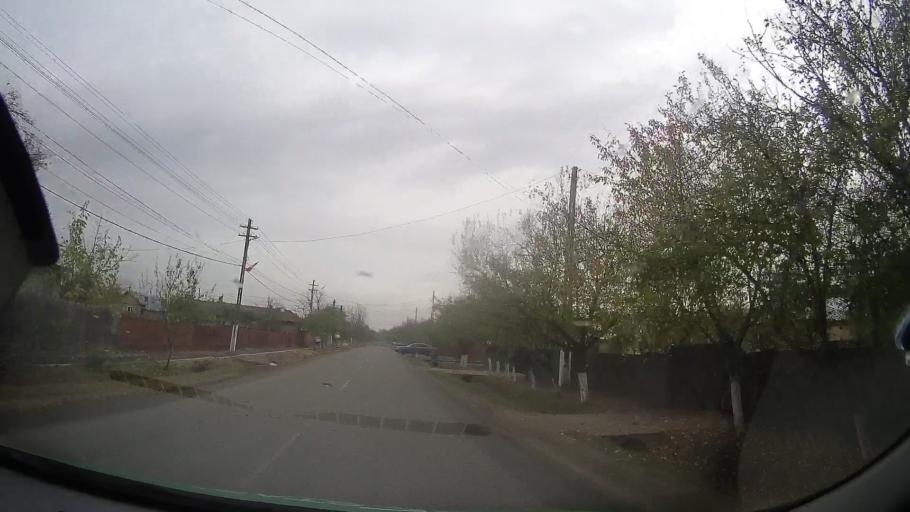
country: RO
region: Prahova
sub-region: Comuna Dumbrava
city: Dumbrava
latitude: 44.8666
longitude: 26.1999
